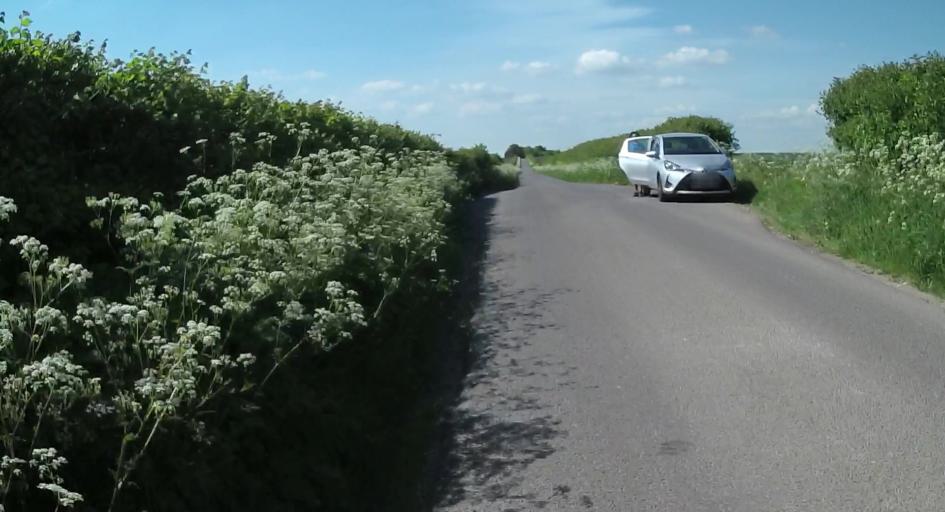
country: GB
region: England
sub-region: Hampshire
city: Kings Worthy
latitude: 51.0749
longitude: -1.2798
